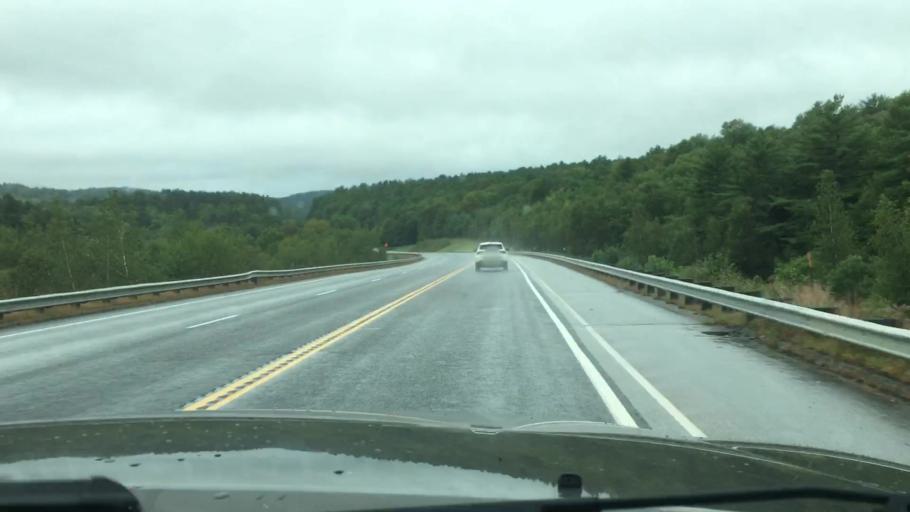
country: US
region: New Hampshire
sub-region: Cheshire County
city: Harrisville
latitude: 43.0061
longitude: -72.1715
